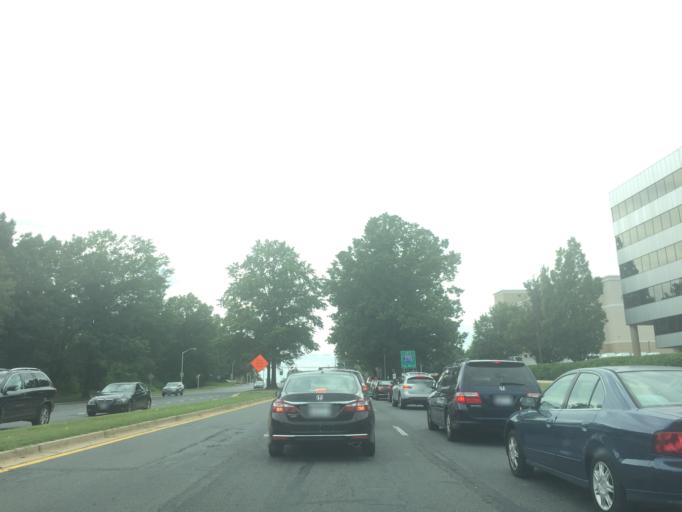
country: US
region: Maryland
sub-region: Montgomery County
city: Gaithersburg
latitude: 39.1544
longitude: -77.2097
